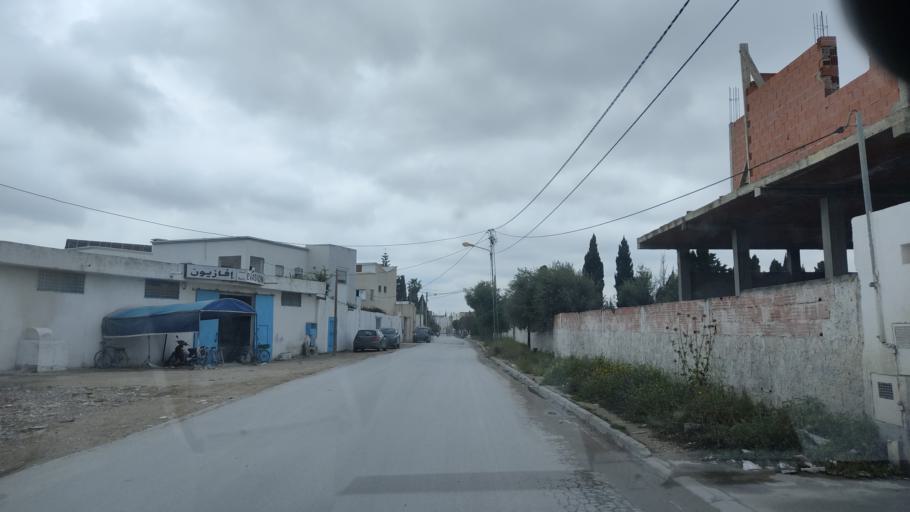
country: TN
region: Ariana
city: Ariana
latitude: 36.8807
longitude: 10.2188
